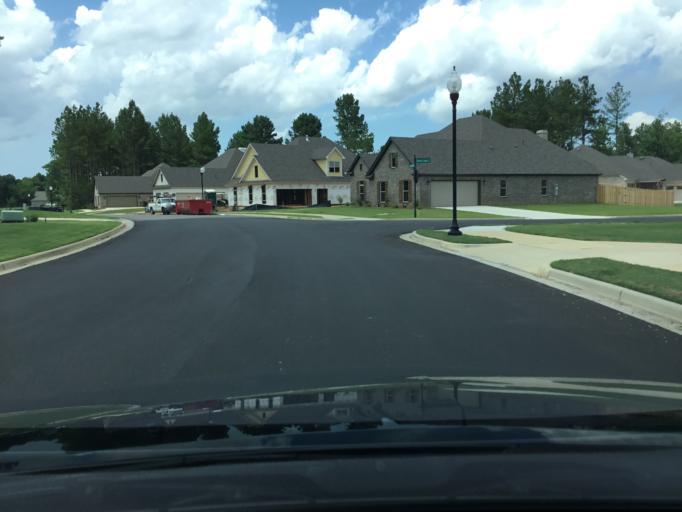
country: US
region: Alabama
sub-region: Montgomery County
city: Pike Road
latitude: 32.3381
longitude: -86.0796
